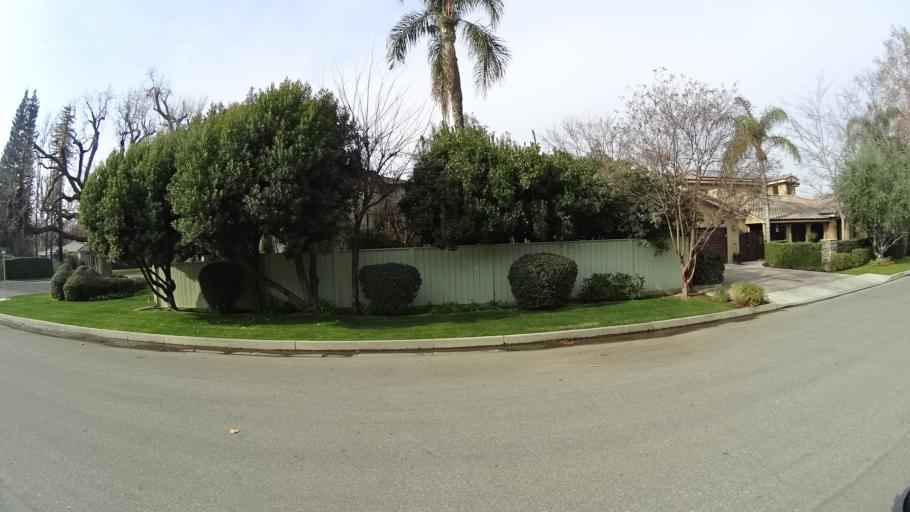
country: US
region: California
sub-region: Kern County
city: Bakersfield
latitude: 35.3795
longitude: -119.0328
